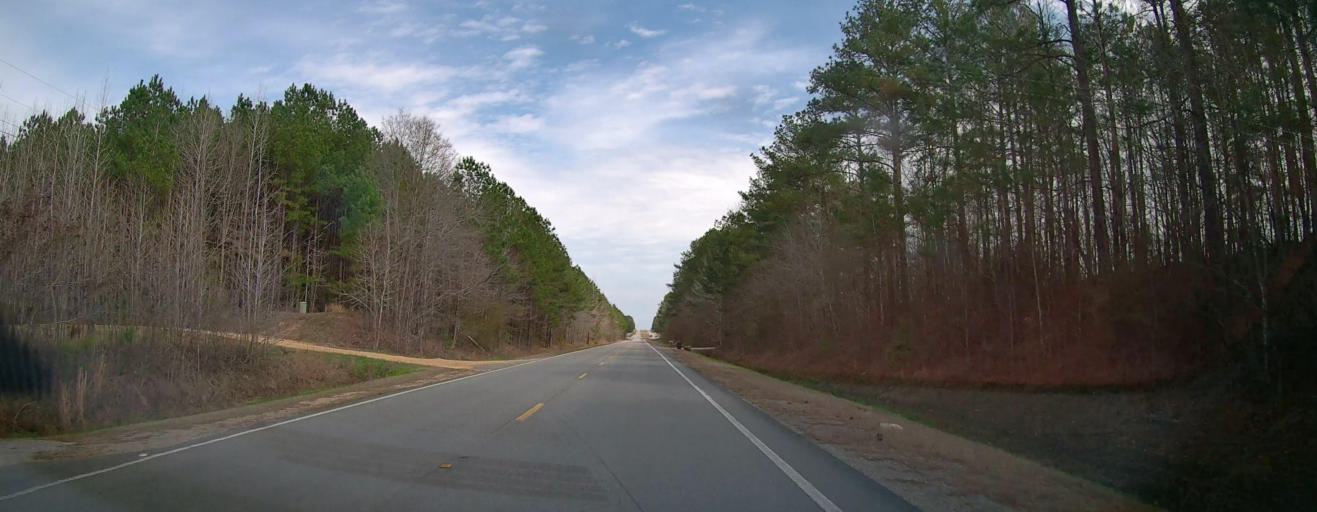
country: US
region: Alabama
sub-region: Marion County
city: Winfield
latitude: 33.9349
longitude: -87.7166
